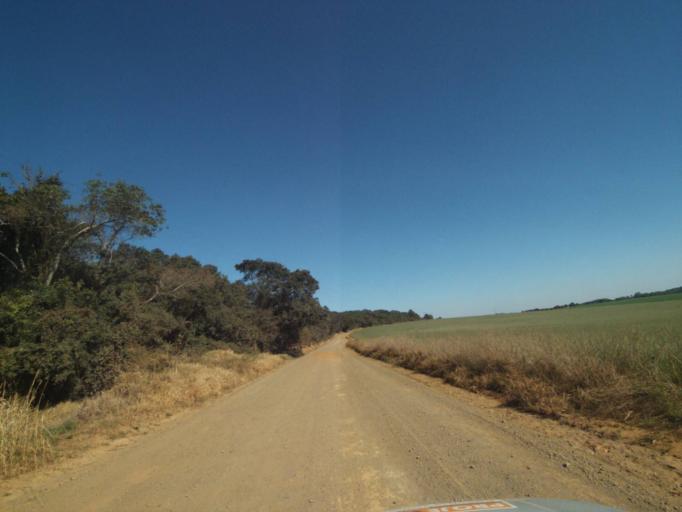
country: BR
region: Parana
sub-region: Tibagi
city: Tibagi
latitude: -24.6232
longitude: -50.6158
